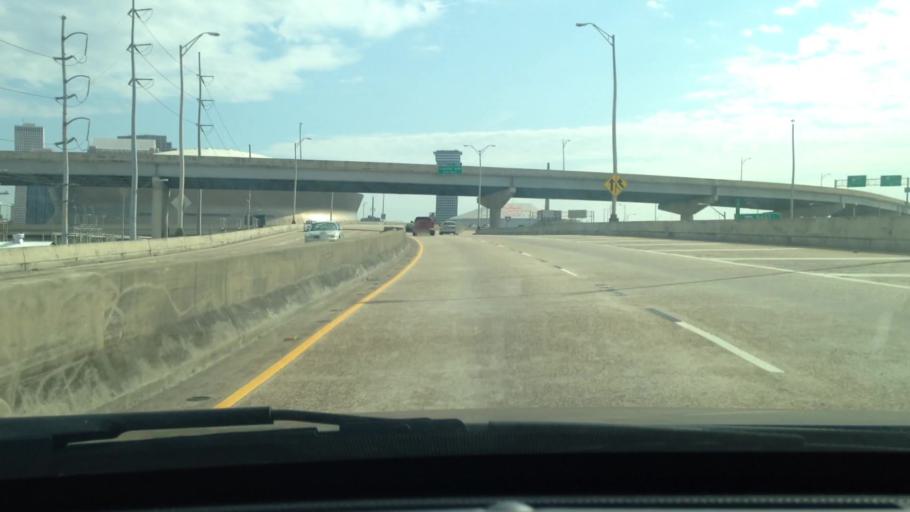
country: US
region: Louisiana
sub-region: Orleans Parish
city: New Orleans
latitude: 29.9536
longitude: -90.0883
